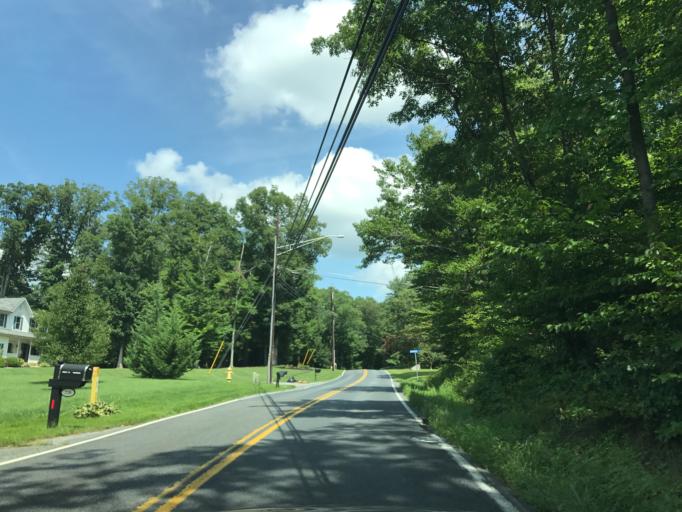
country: US
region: Maryland
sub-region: Harford County
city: Bel Air South
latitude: 39.4780
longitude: -76.2935
